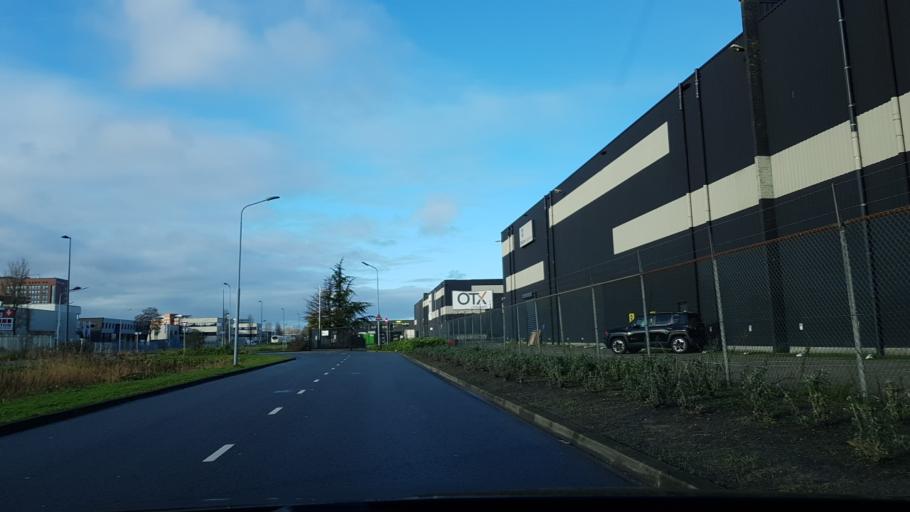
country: NL
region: North Holland
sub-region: Gemeente Haarlemmermeer
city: Hoofddorp
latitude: 52.2923
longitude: 4.7230
